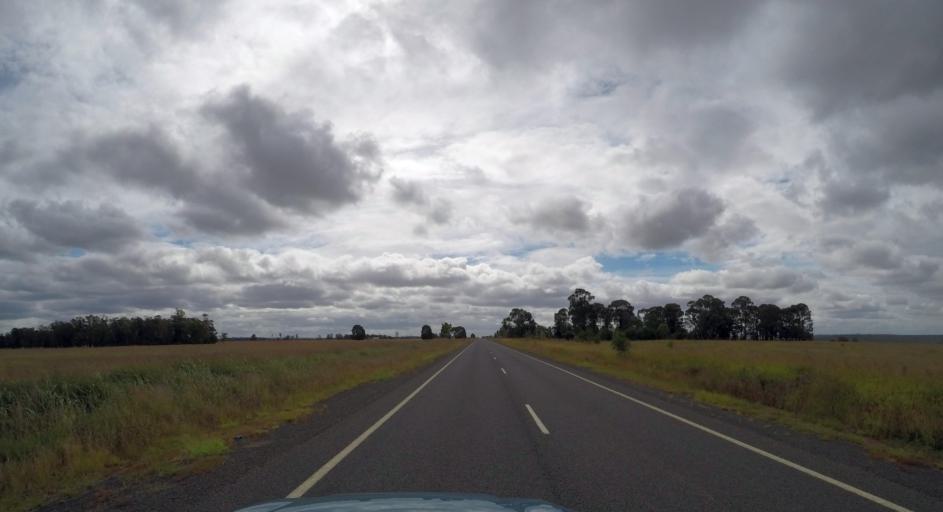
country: AU
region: Queensland
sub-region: South Burnett
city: Kingaroy
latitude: -26.3850
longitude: 151.2452
